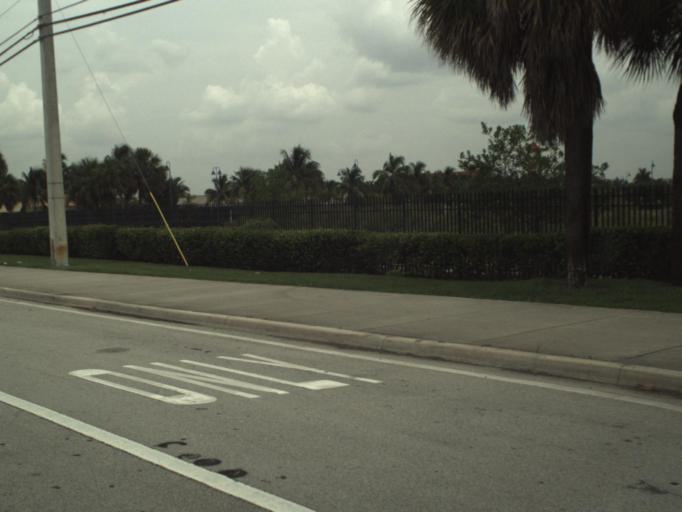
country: US
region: Florida
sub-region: Broward County
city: Broward Estates
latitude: 26.1362
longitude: -80.1970
